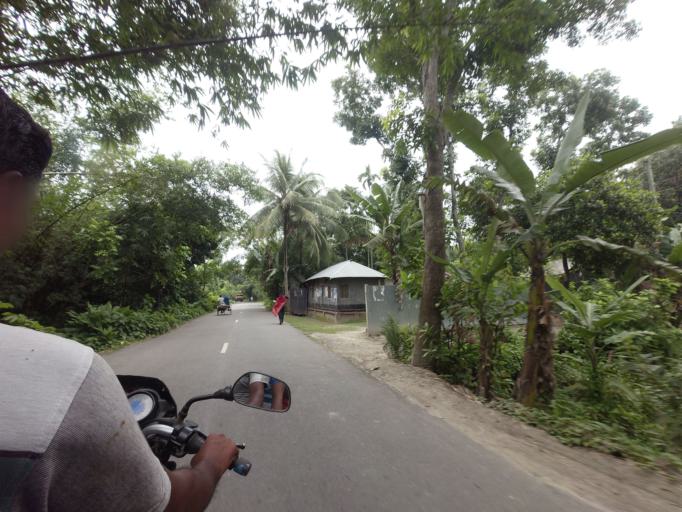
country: BD
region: Khulna
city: Kalia
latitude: 23.1585
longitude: 89.6439
